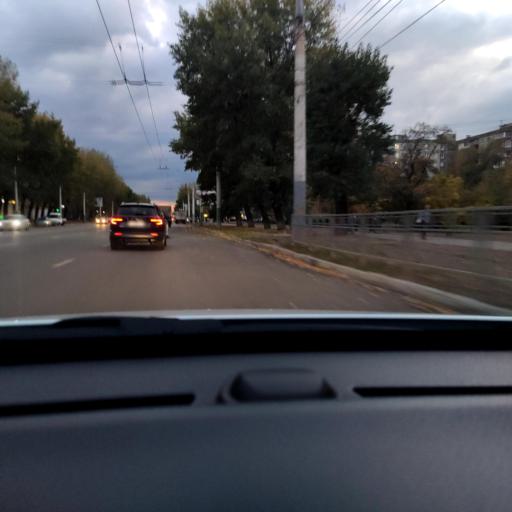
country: RU
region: Voronezj
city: Voronezh
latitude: 51.6462
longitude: 39.2390
